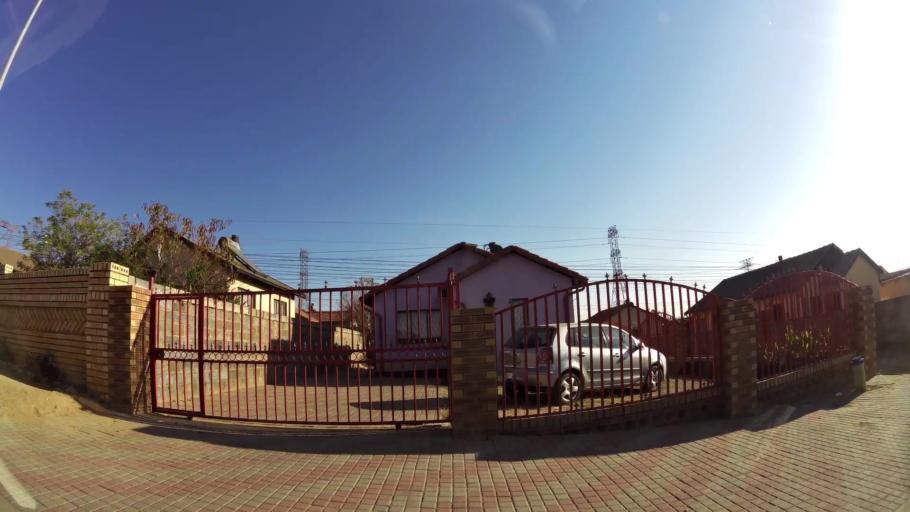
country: ZA
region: Gauteng
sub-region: City of Johannesburg Metropolitan Municipality
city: Modderfontein
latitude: -26.0423
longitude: 28.1524
